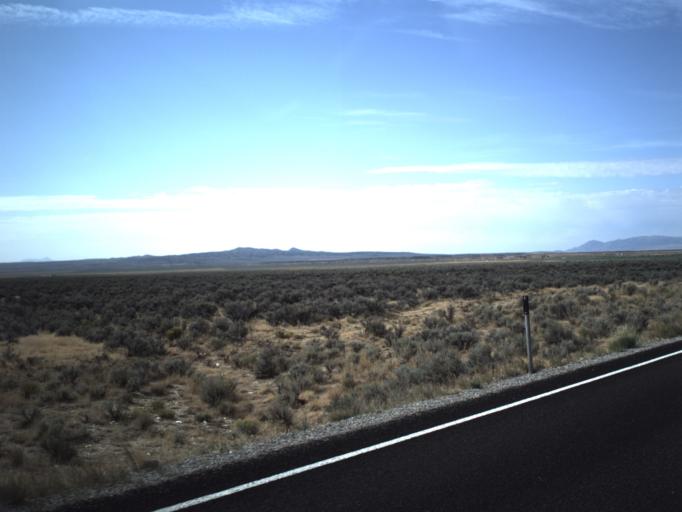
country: US
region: Idaho
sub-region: Cassia County
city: Burley
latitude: 41.7926
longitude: -113.4692
